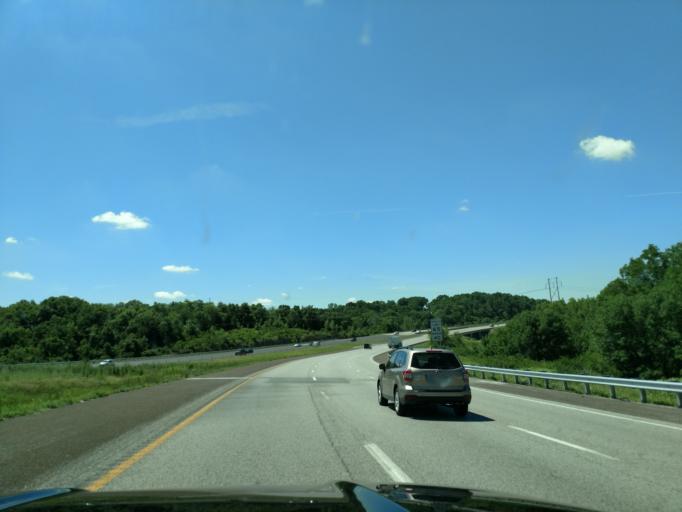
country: US
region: Missouri
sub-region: Jackson County
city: Raytown
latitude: 39.0151
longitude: -94.4979
